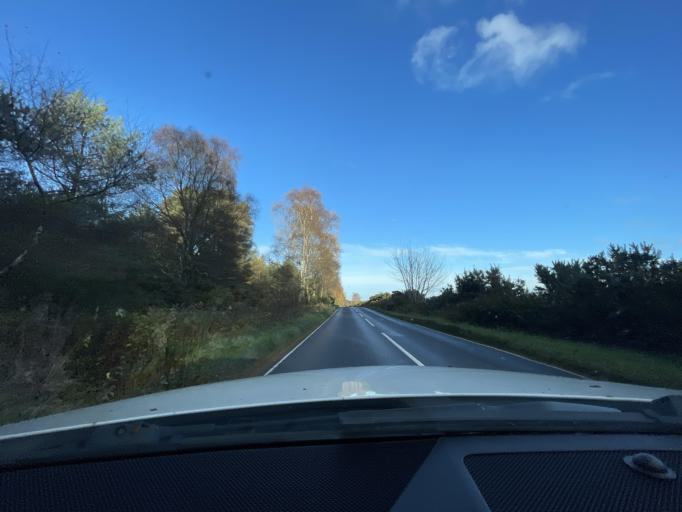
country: GB
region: Scotland
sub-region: Highland
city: Inverness
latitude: 57.4159
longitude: -4.3028
